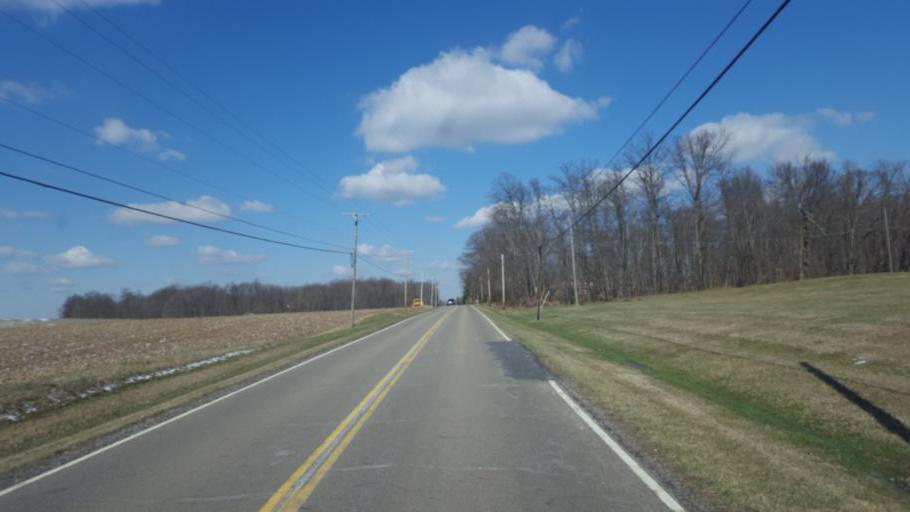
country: US
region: Ohio
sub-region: Licking County
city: Utica
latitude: 40.2372
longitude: -82.4761
